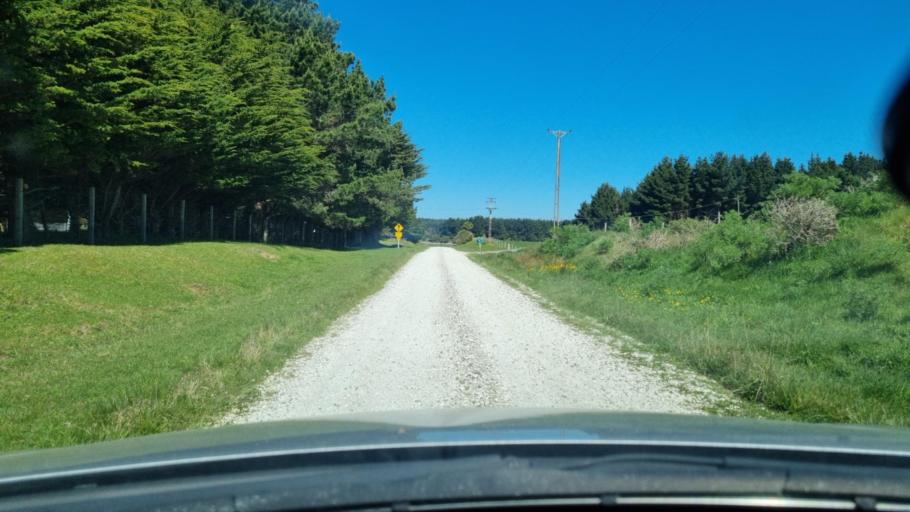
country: NZ
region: Southland
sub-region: Invercargill City
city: Invercargill
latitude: -46.4573
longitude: 168.2719
